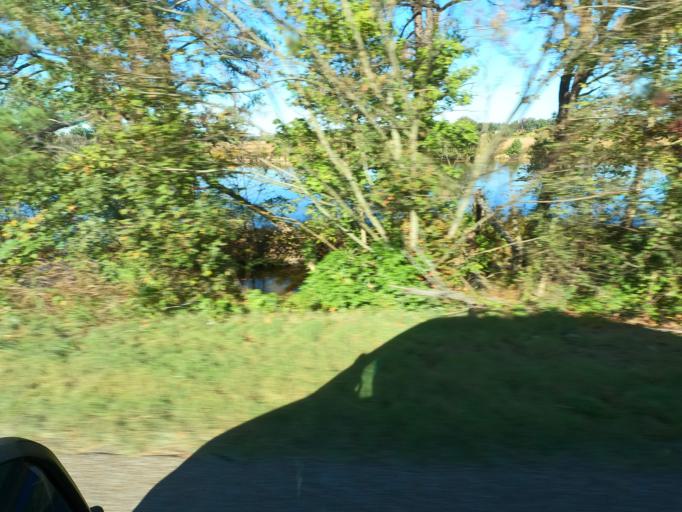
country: US
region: Tennessee
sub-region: Tipton County
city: Brighton
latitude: 35.4995
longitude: -89.7203
